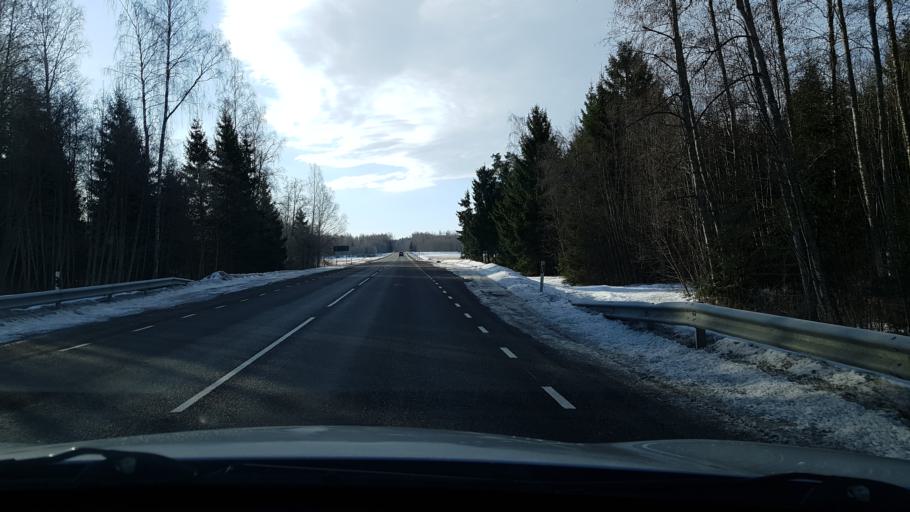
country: EE
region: Viljandimaa
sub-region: Vohma linn
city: Vohma
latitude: 58.5898
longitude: 25.5713
